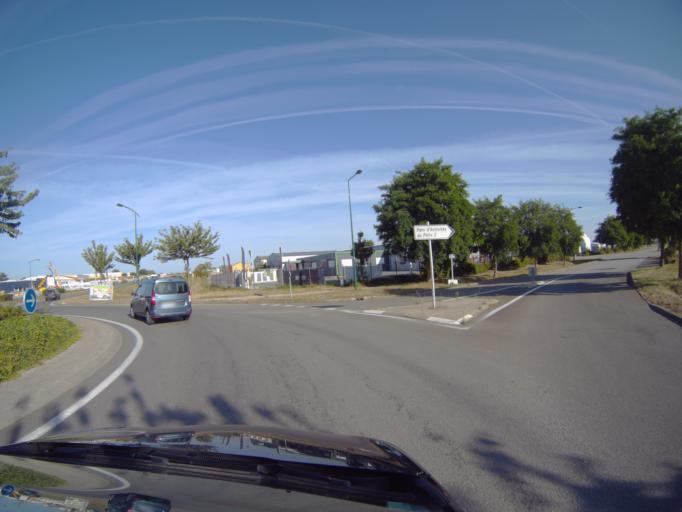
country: FR
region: Pays de la Loire
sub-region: Departement de la Vendee
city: Saint-Hilaire-de-Talmont
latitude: 46.4544
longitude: -1.5953
